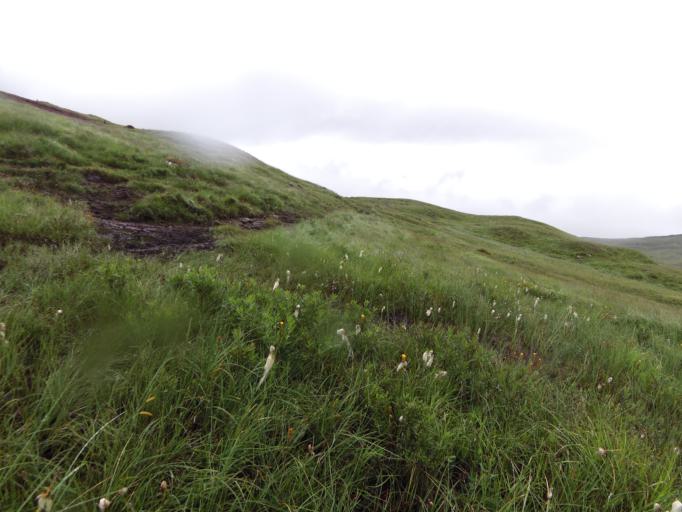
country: GB
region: Scotland
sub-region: Highland
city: Spean Bridge
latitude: 56.7737
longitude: -4.7131
